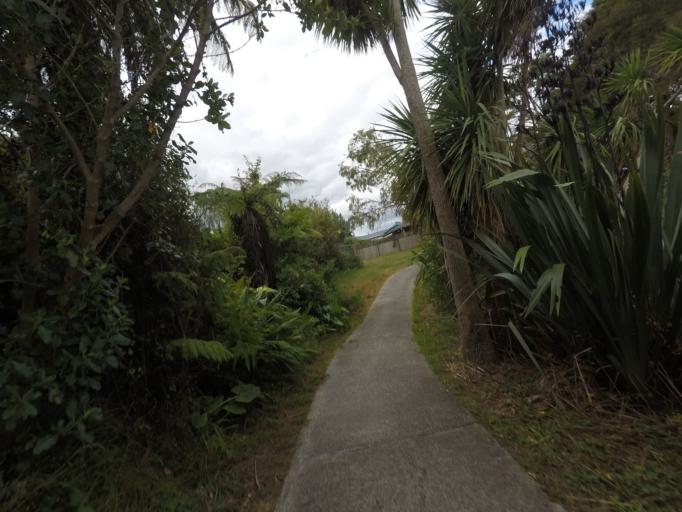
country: NZ
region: Auckland
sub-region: Auckland
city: Papakura
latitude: -37.0603
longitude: 174.9331
